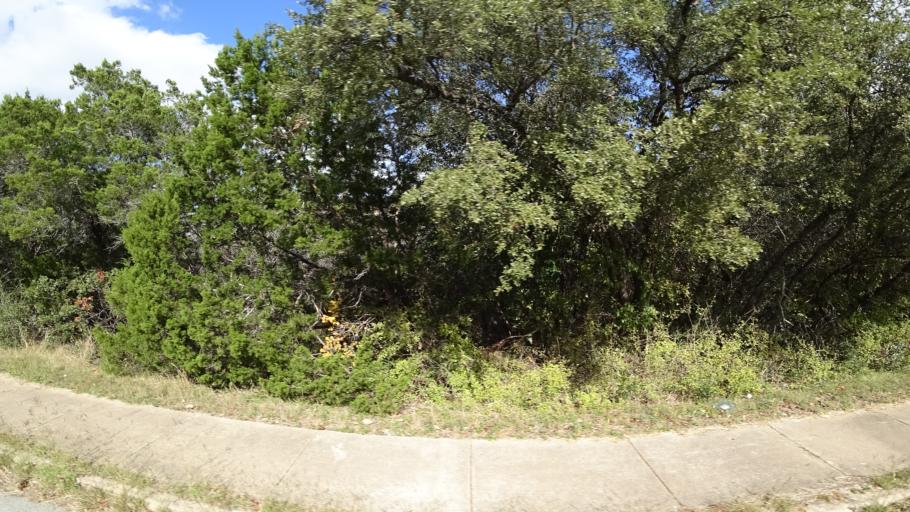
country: US
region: Texas
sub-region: Williamson County
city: Jollyville
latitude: 30.4279
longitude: -97.7818
